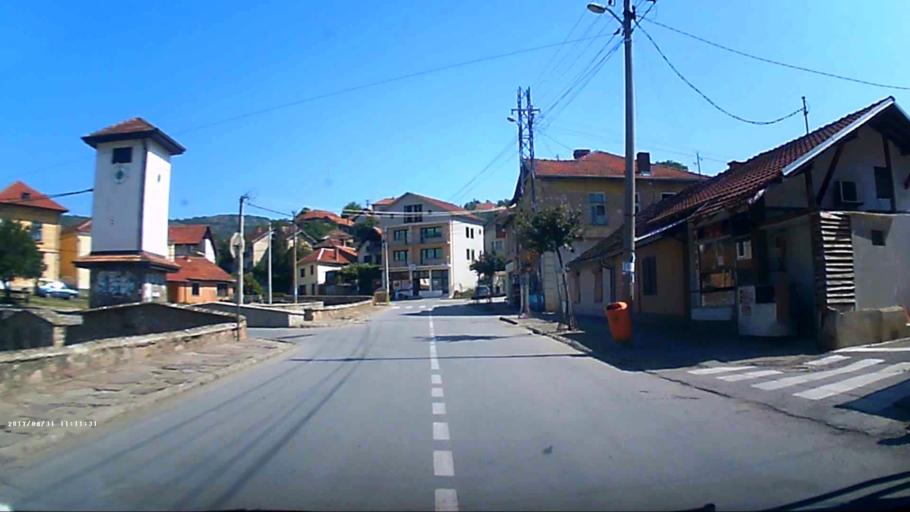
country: RS
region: Central Serbia
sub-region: Pirotski Okrug
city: Dimitrovgrad
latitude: 43.0180
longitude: 22.7812
